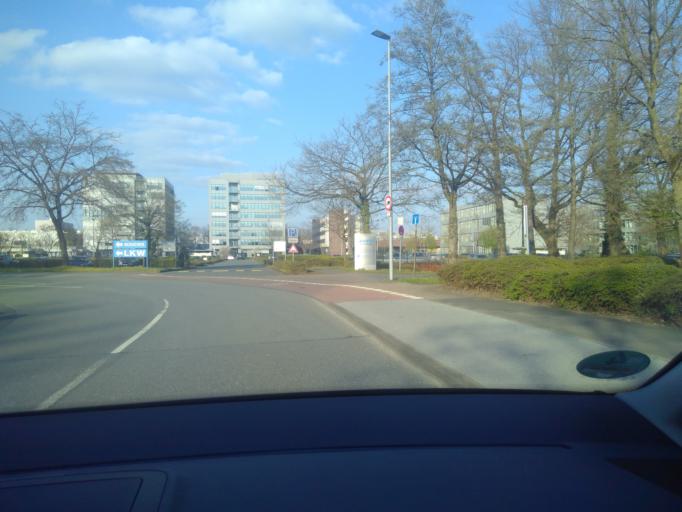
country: DE
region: North Rhine-Westphalia
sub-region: Regierungsbezirk Detmold
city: Guetersloh
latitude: 51.8826
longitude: 8.4418
